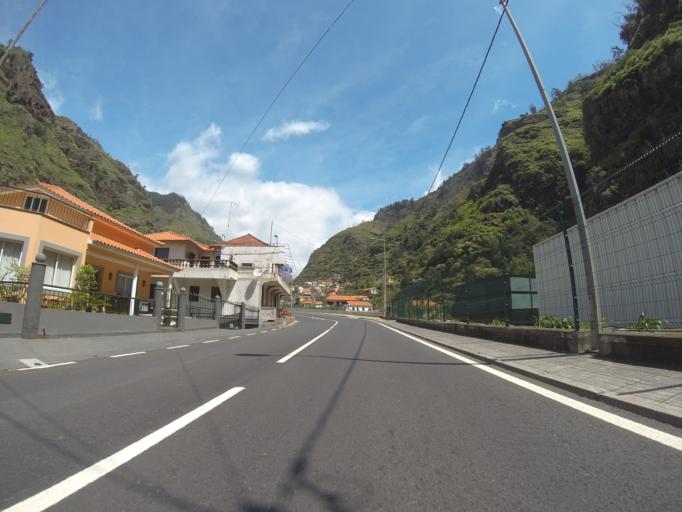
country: PT
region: Madeira
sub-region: Ribeira Brava
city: Campanario
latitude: 32.6855
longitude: -17.0506
